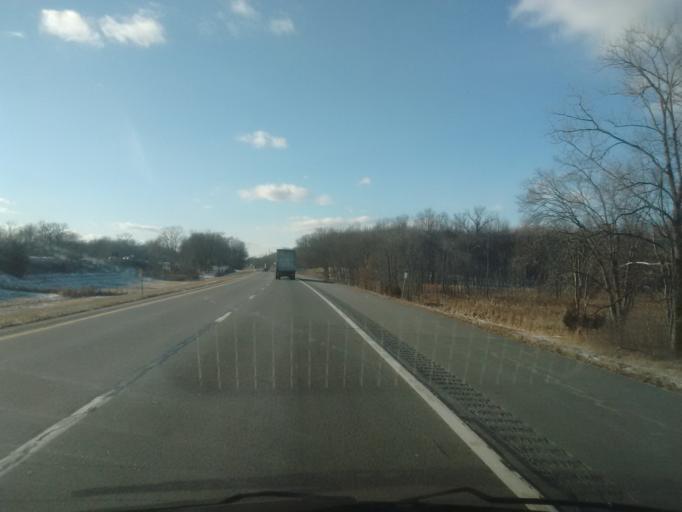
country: US
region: New York
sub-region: Orange County
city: Walden
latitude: 41.5175
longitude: -74.1697
